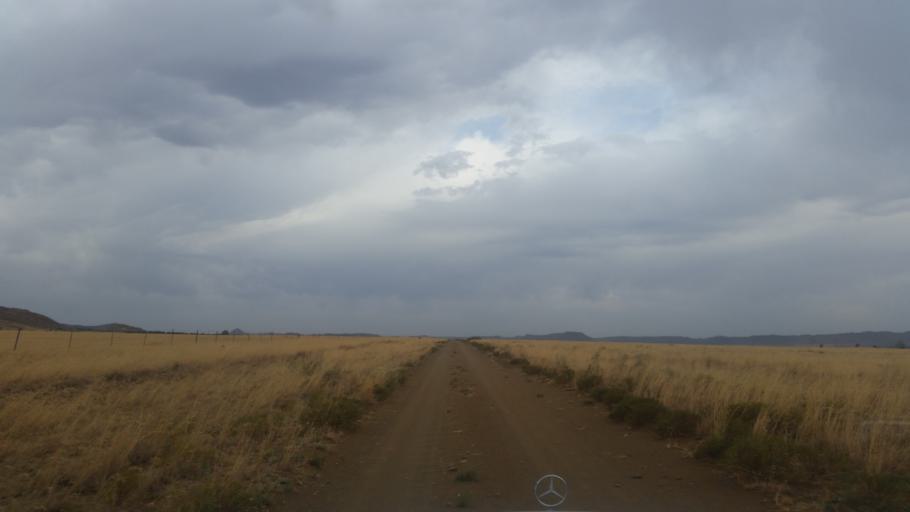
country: ZA
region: Orange Free State
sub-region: Xhariep District Municipality
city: Trompsburg
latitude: -30.5069
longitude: 25.9232
